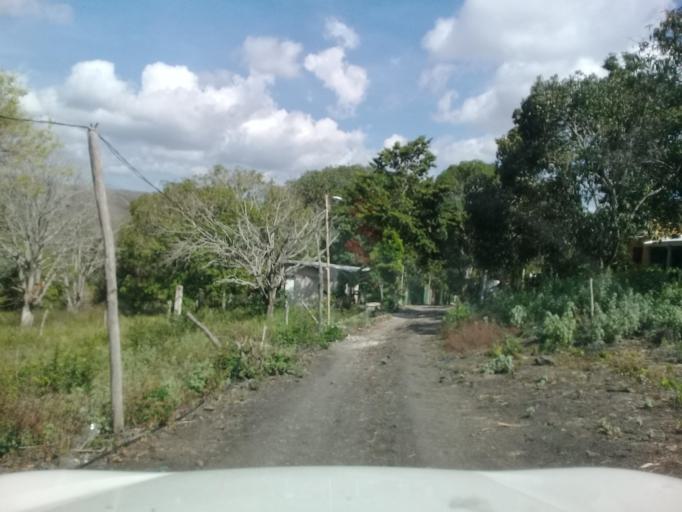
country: MX
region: Veracruz
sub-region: Emiliano Zapata
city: Plan del Rio
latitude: 19.4013
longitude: -96.6473
